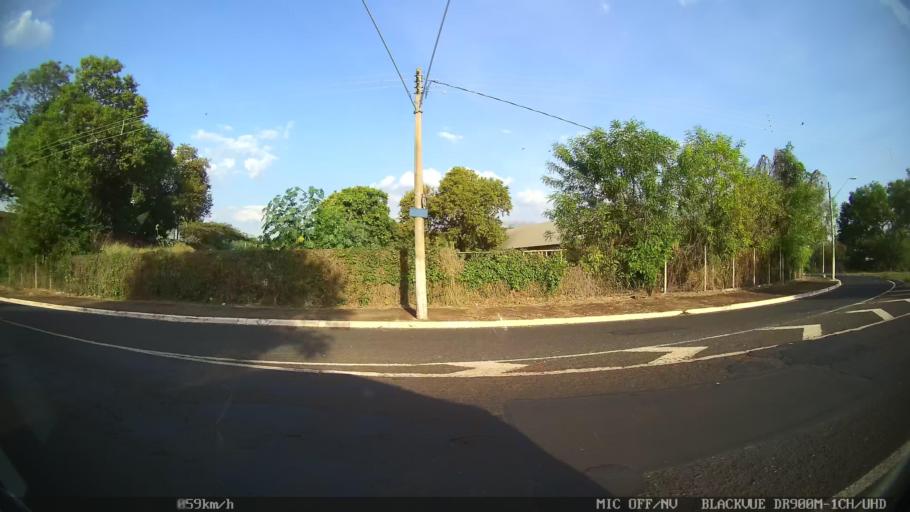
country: BR
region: Sao Paulo
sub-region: Ribeirao Preto
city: Ribeirao Preto
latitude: -21.1608
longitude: -47.8143
